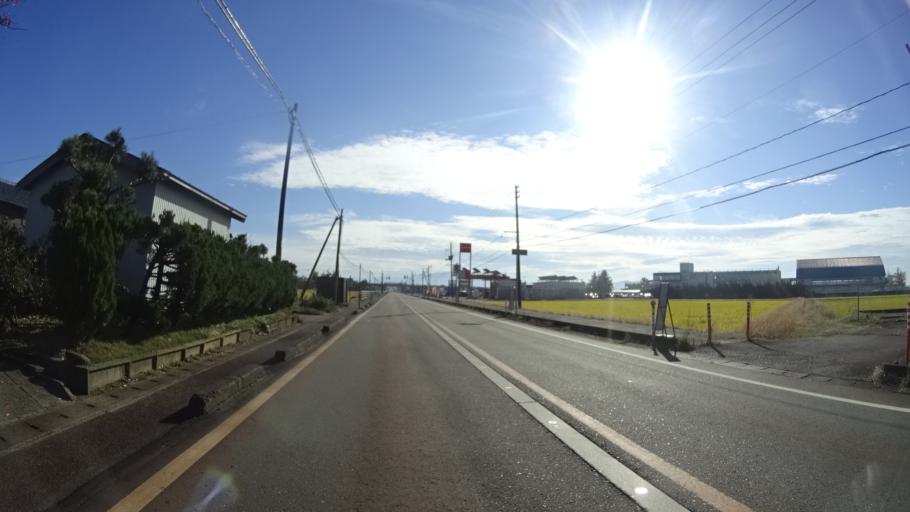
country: JP
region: Niigata
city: Mitsuke
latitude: 37.5511
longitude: 138.8683
